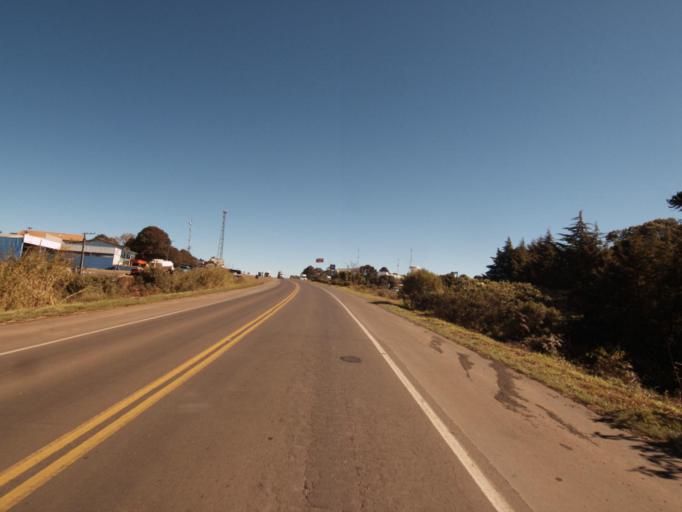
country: BR
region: Santa Catarina
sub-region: Xanxere
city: Xanxere
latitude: -26.8555
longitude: -52.2557
